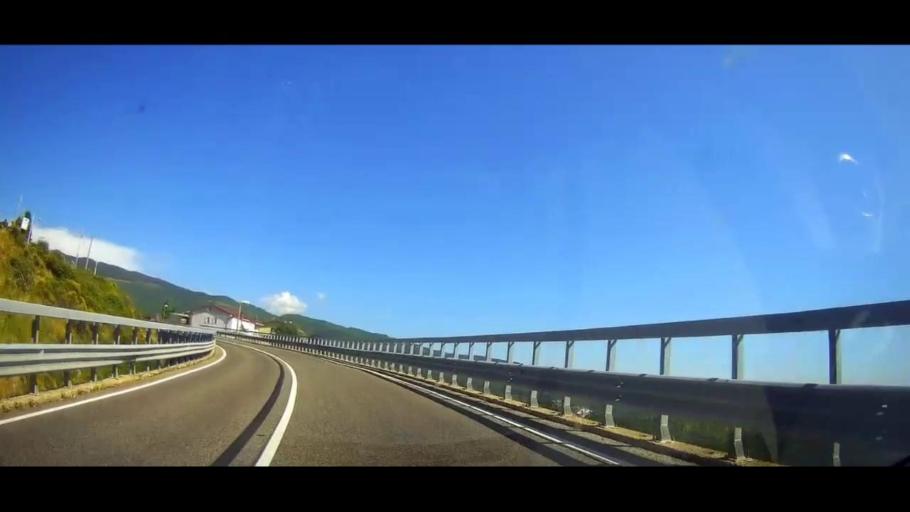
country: IT
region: Calabria
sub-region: Provincia di Cosenza
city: Spezzano Piccolo
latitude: 39.2945
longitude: 16.3450
